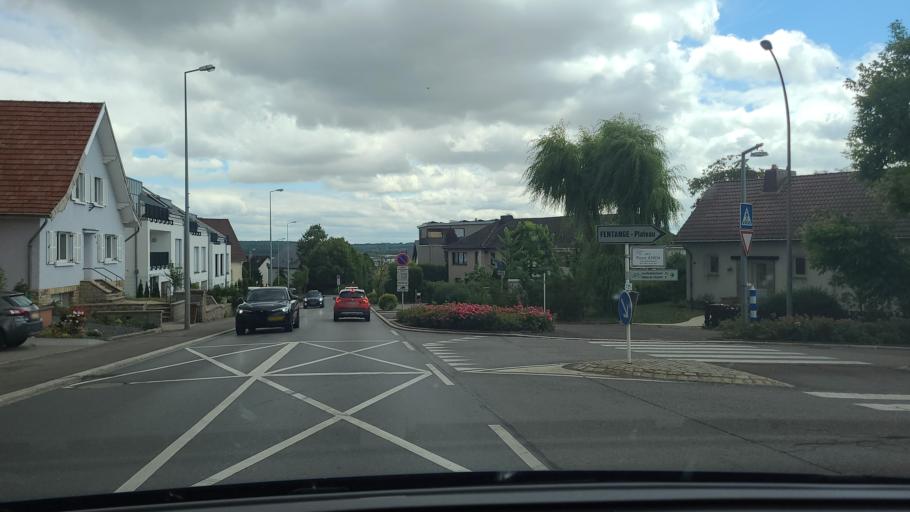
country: LU
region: Luxembourg
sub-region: Canton de Luxembourg
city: Hesperange
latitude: 49.5719
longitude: 6.1449
